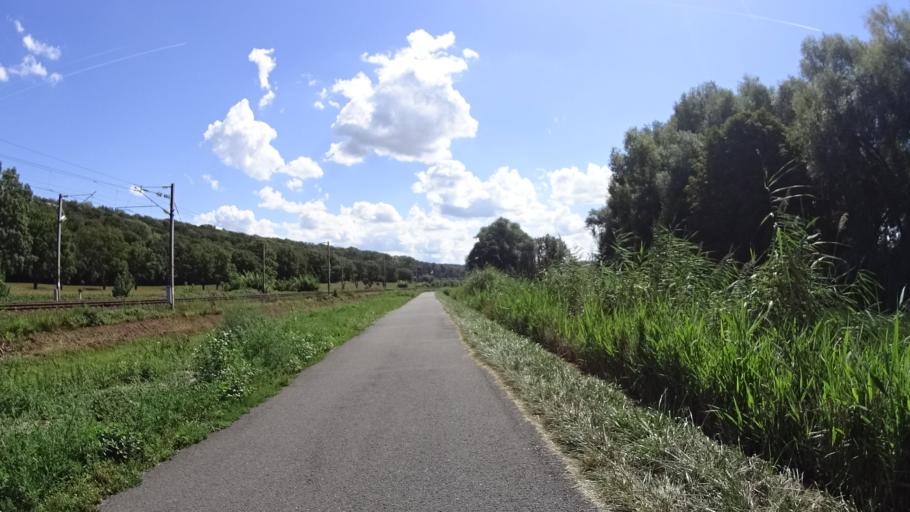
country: FR
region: Alsace
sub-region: Departement du Haut-Rhin
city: Flaxlanden
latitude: 47.7069
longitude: 7.3105
